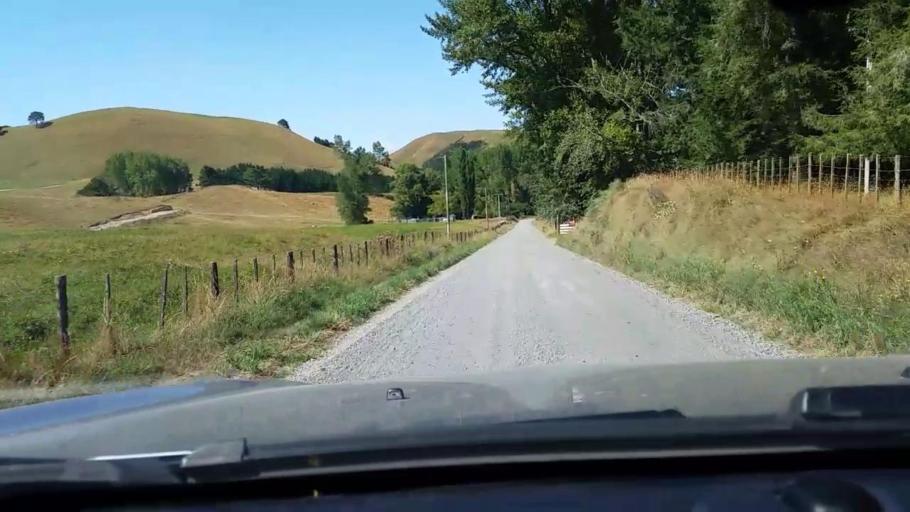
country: NZ
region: Bay of Plenty
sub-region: Rotorua District
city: Rotorua
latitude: -38.3706
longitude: 176.2069
